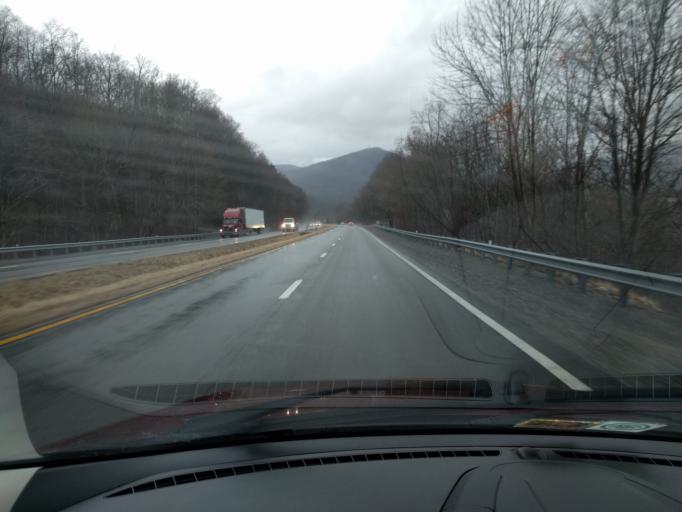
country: US
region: Virginia
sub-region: Montgomery County
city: Prices Fork
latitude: 37.2867
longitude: -80.4834
